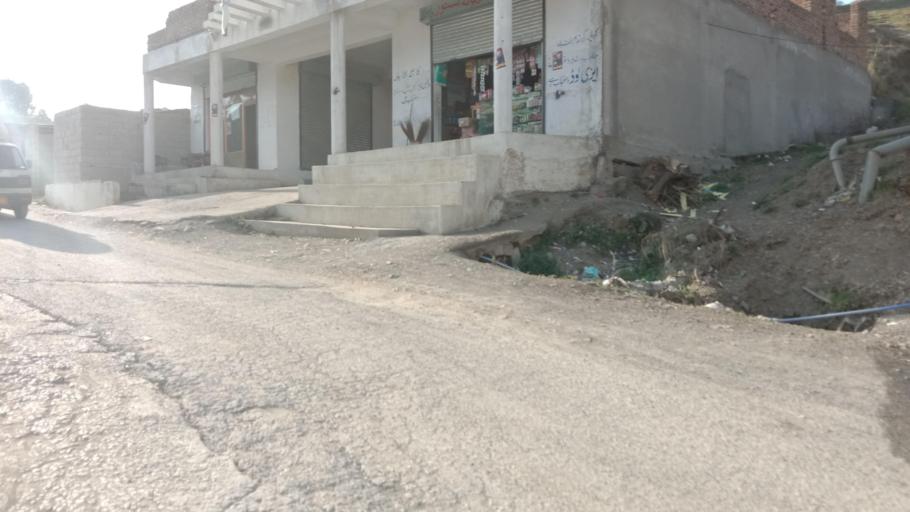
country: PK
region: Khyber Pakhtunkhwa
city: Abbottabad
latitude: 34.2036
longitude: 73.2217
